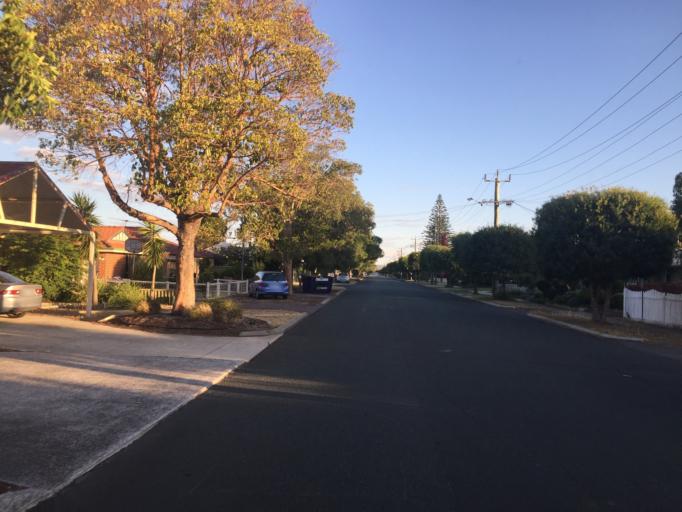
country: AU
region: Western Australia
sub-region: Belmont
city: Rivervale
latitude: -31.9607
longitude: 115.9209
